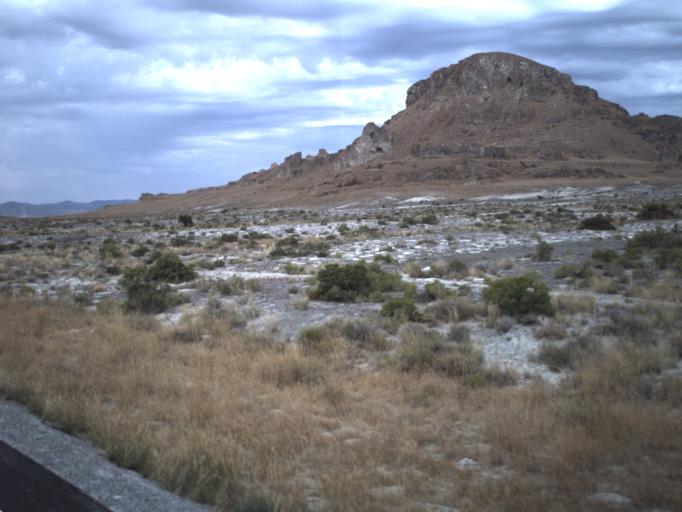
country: US
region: Utah
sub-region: Tooele County
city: Wendover
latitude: 41.4285
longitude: -113.8233
